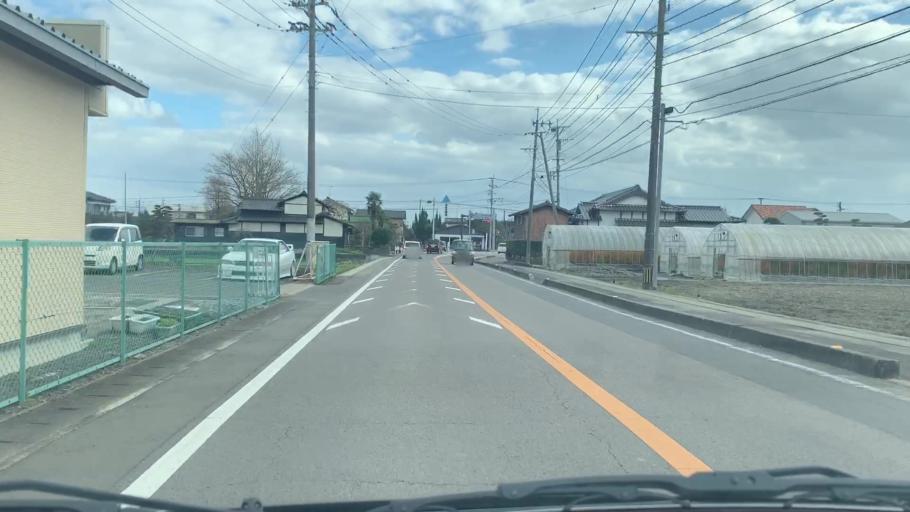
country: JP
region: Saga Prefecture
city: Kashima
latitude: 33.1905
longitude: 130.1319
